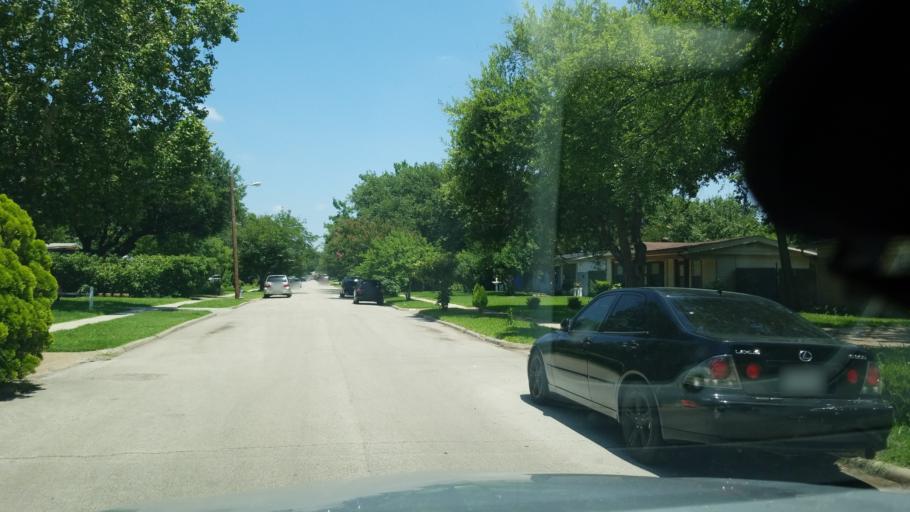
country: US
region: Texas
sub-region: Dallas County
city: Irving
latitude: 32.8280
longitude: -96.9692
